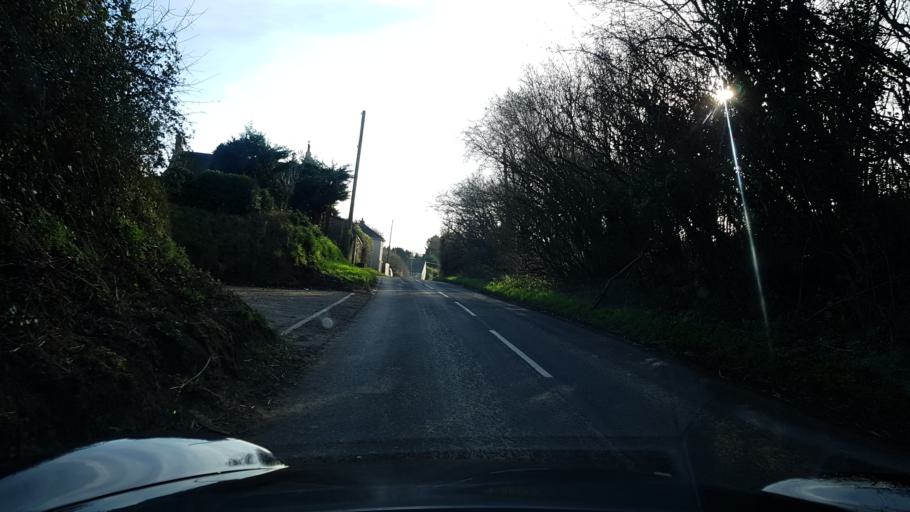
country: GB
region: England
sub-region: Dorset
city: Bridport
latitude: 50.7483
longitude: -2.7690
